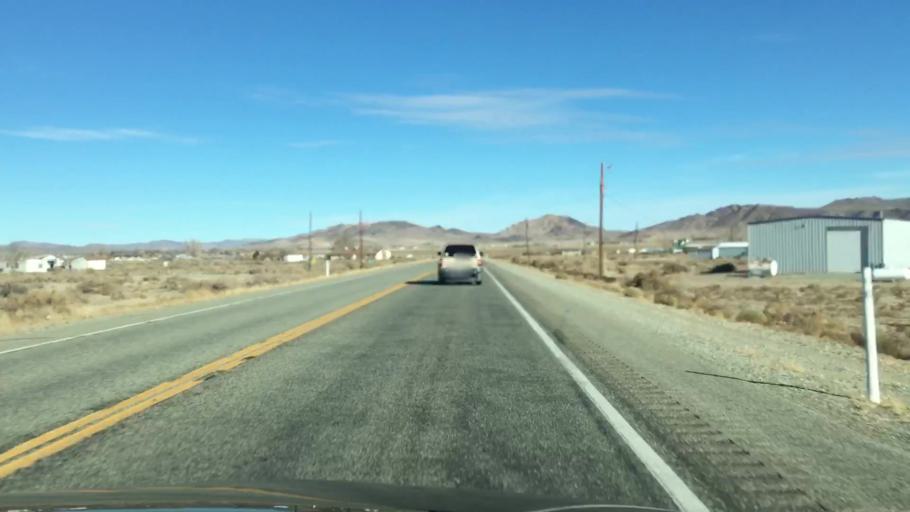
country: US
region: Nevada
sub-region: Lyon County
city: Yerington
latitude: 39.0108
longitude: -119.0767
